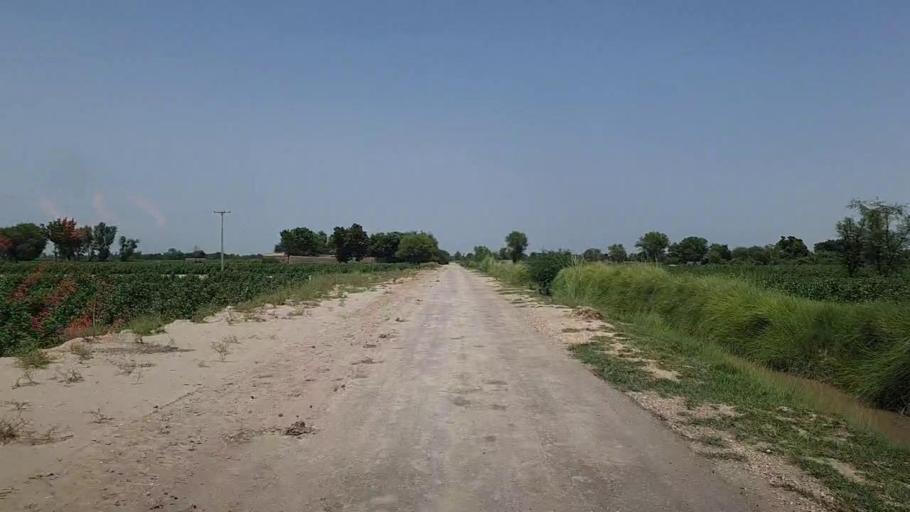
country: PK
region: Sindh
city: Pad Idan
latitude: 26.7534
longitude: 68.3168
